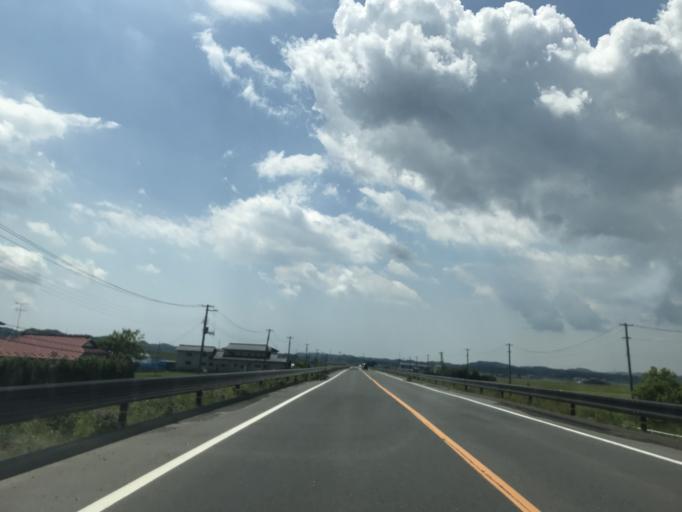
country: JP
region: Miyagi
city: Matsushima
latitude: 38.4591
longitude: 141.0868
